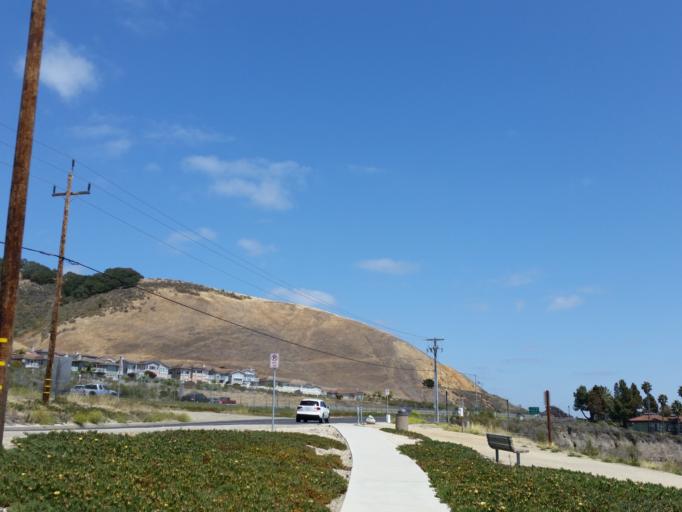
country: US
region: California
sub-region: San Luis Obispo County
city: Pismo Beach
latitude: 35.1540
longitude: -120.6636
